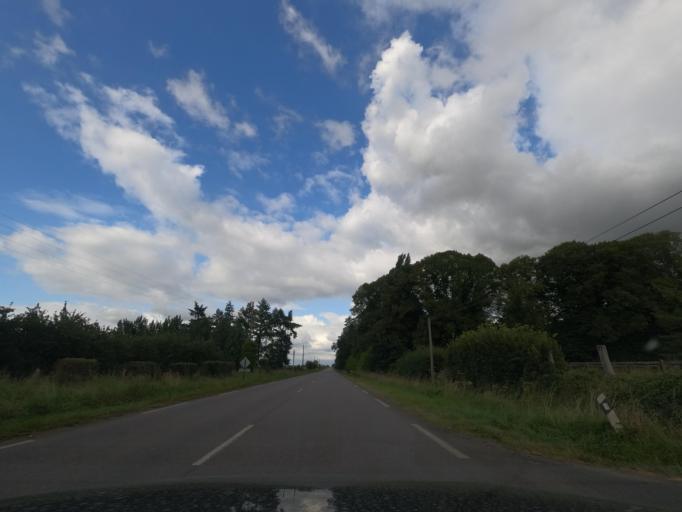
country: FR
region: Lower Normandy
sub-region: Departement du Calvados
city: Orbec
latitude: 48.9582
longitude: 0.4689
